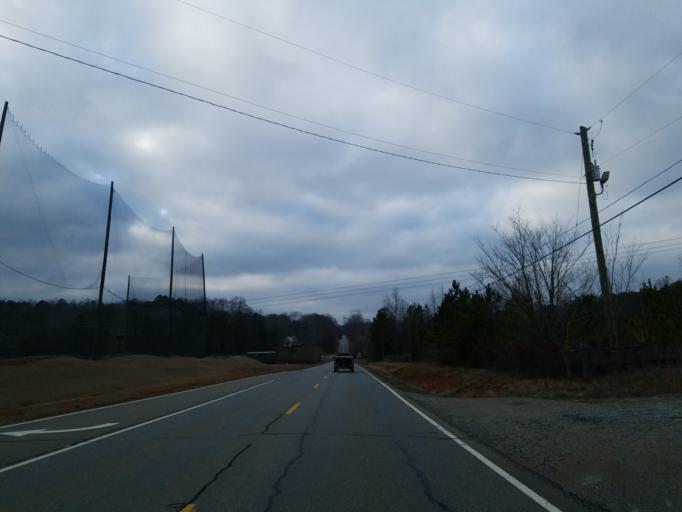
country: US
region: Georgia
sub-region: Cherokee County
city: Canton
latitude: 34.3027
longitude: -84.5236
